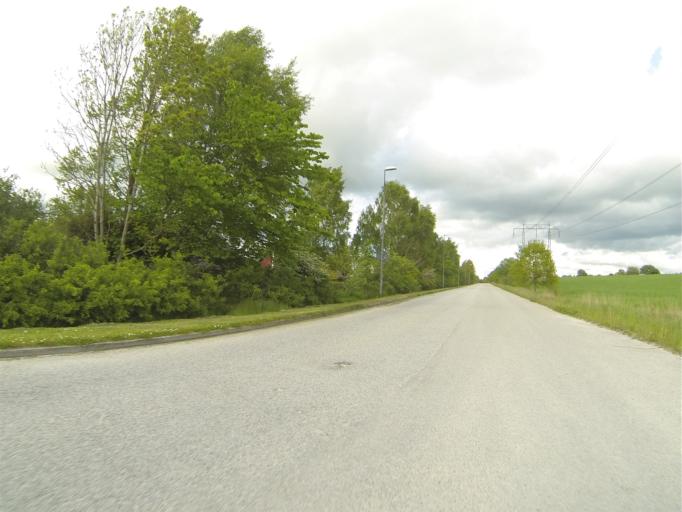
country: SE
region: Skane
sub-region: Lunds Kommun
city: Genarp
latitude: 55.7054
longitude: 13.3283
